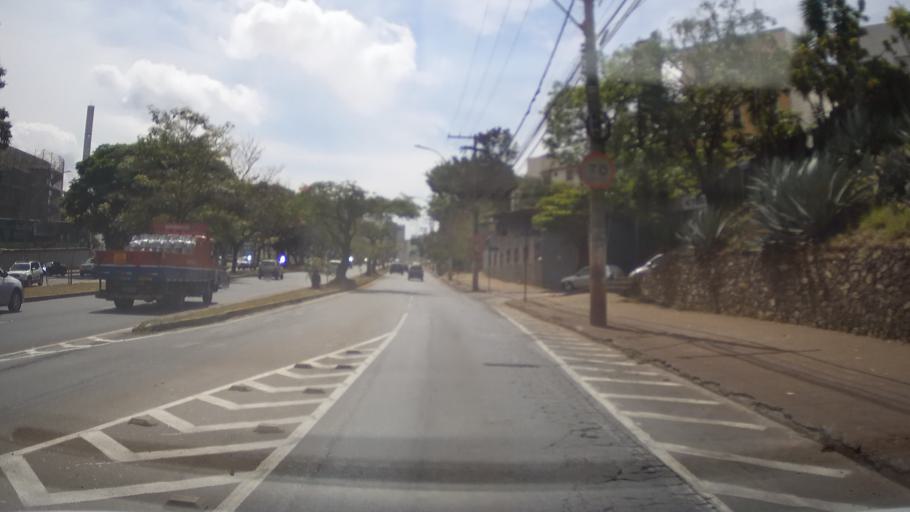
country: BR
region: Minas Gerais
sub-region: Belo Horizonte
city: Belo Horizonte
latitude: -19.9721
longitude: -43.9494
